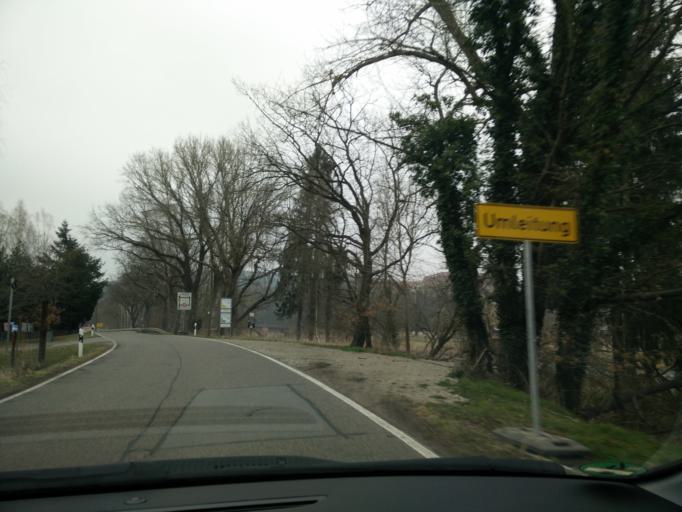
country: DE
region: Saxony
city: Wechselburg
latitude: 51.0006
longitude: 12.7696
